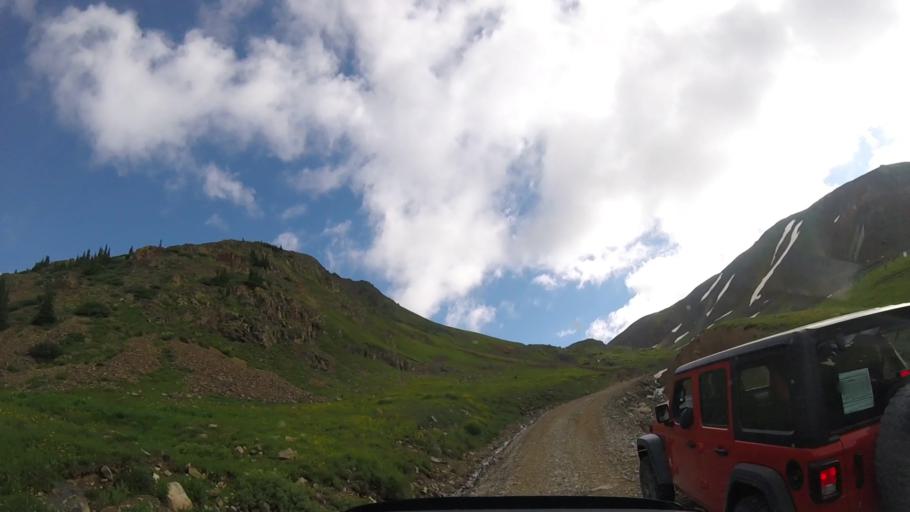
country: US
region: Colorado
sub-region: San Juan County
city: Silverton
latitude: 37.9125
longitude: -107.6327
